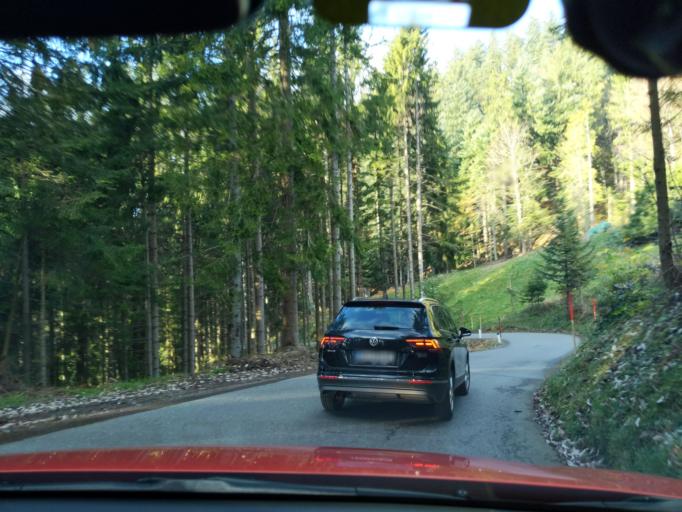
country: AT
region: Vorarlberg
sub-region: Politischer Bezirk Bregenz
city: Eichenberg
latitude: 47.5155
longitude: 9.7796
